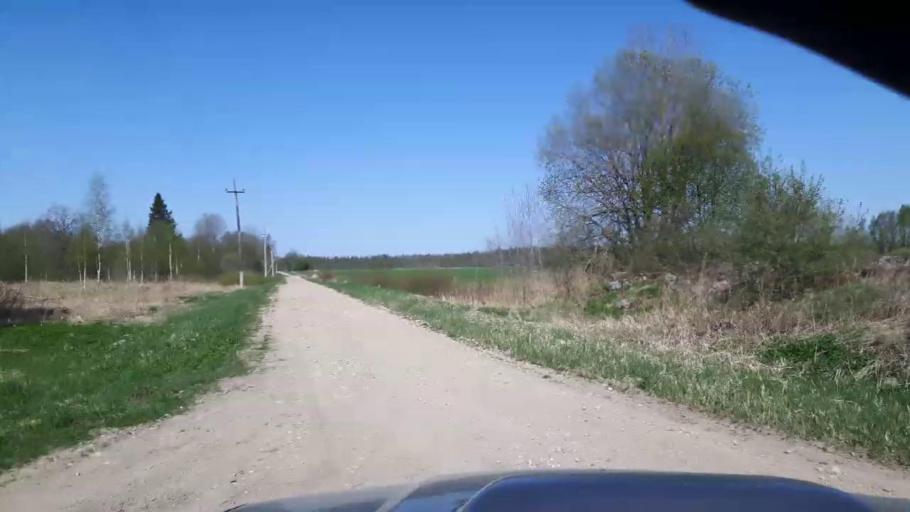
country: EE
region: Paernumaa
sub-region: Tootsi vald
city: Tootsi
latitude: 58.4448
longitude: 24.8119
